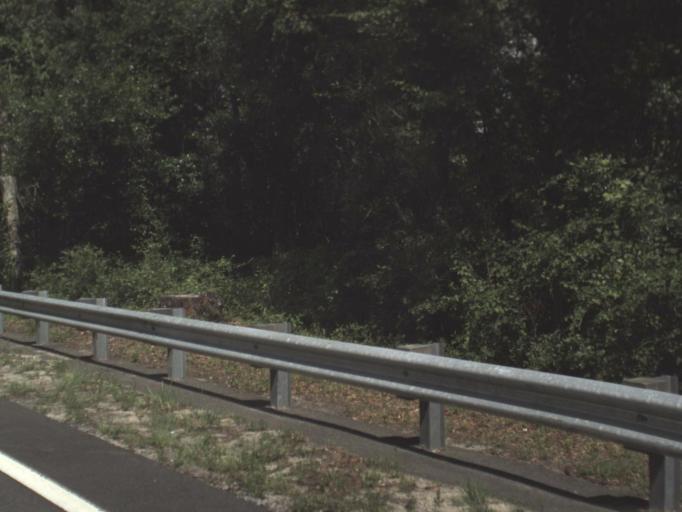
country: US
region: Florida
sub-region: Clay County
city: Keystone Heights
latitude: 29.7249
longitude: -81.9888
